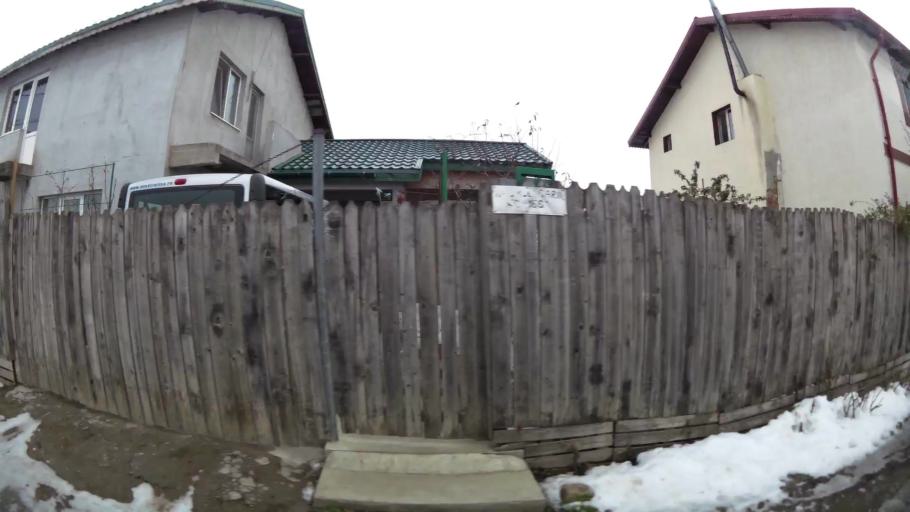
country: RO
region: Ilfov
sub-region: Comuna Pantelimon
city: Pantelimon
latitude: 44.4645
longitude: 26.2041
